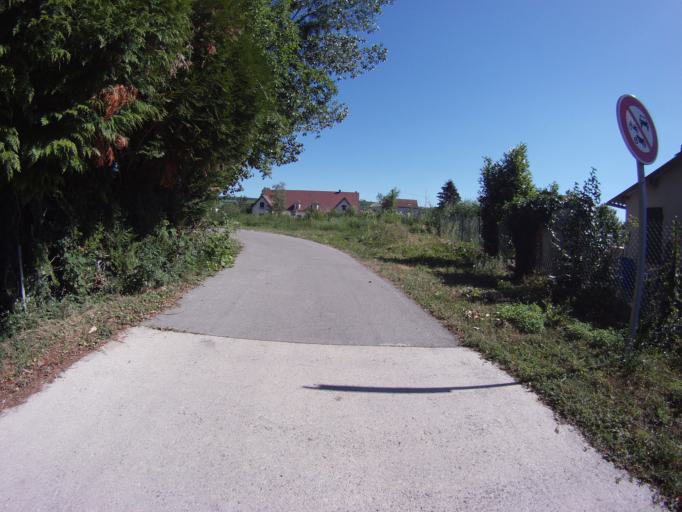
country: FR
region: Champagne-Ardenne
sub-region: Departement de la Marne
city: Ay
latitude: 49.0525
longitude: 3.9969
